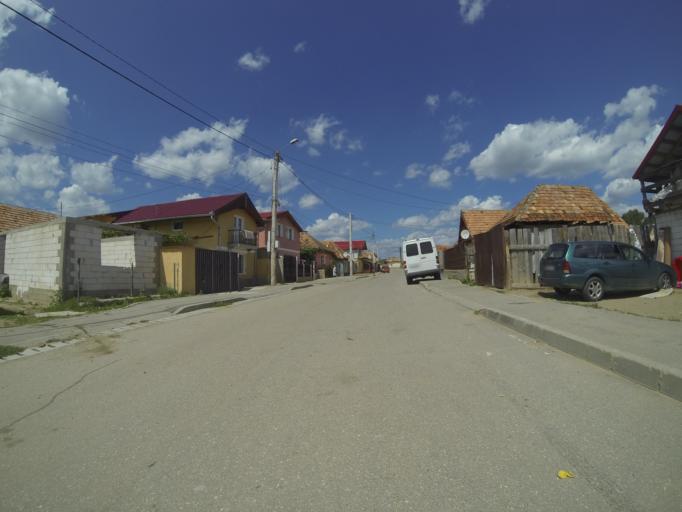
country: RO
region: Brasov
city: Fogarasch
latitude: 45.8561
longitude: 24.9829
